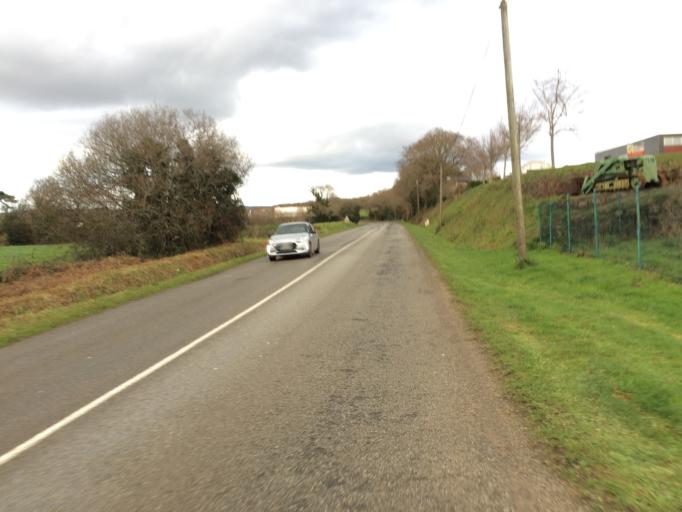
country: FR
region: Brittany
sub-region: Departement du Finistere
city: Daoulas
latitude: 48.3492
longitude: -4.2556
